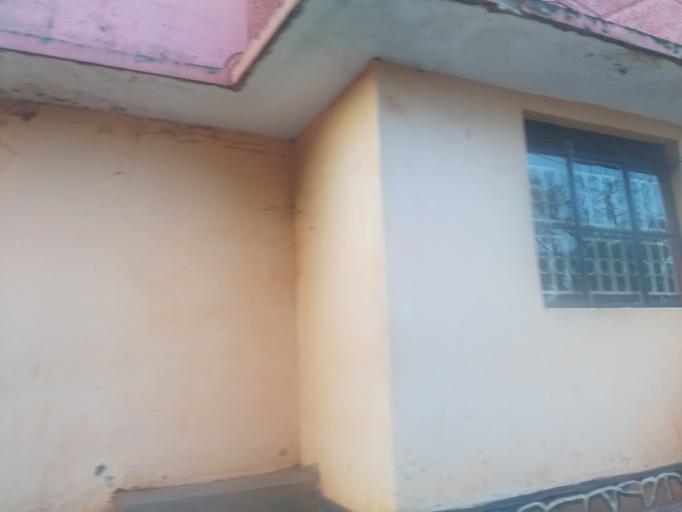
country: UG
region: Central Region
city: Kampala Central Division
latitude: 0.3391
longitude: 32.5837
